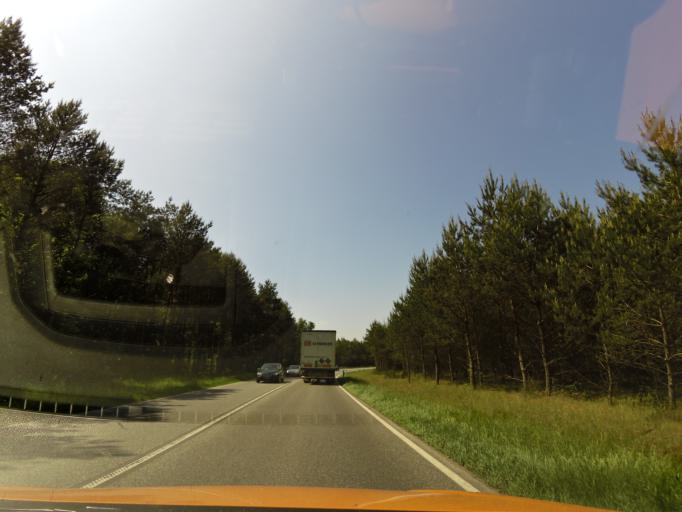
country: DE
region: Mecklenburg-Vorpommern
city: Selmsdorf
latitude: 53.8723
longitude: 10.7819
